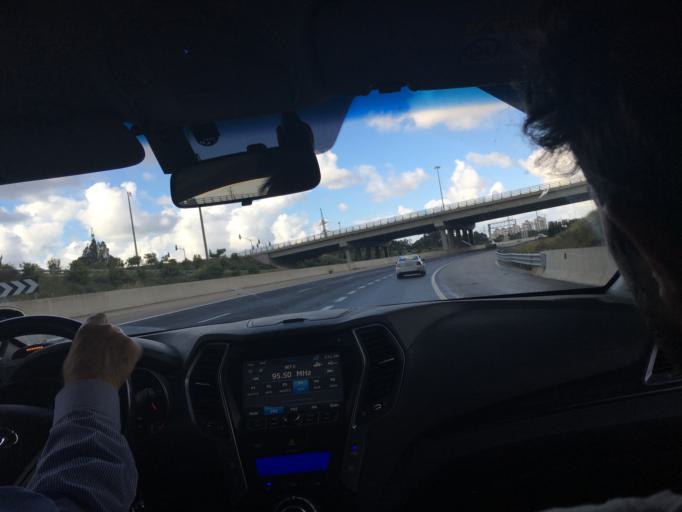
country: IL
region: Central District
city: Rishon LeZiyyon
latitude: 31.9546
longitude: 34.7856
